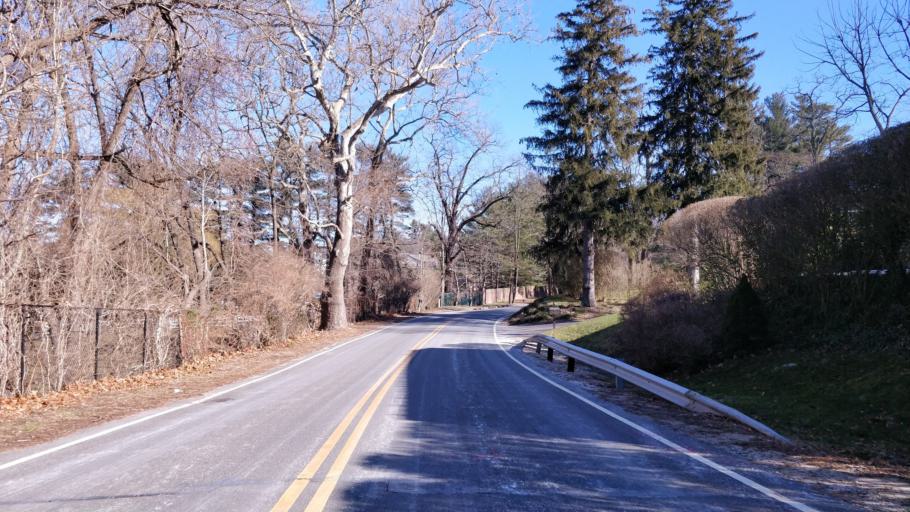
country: US
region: New York
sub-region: Nassau County
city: Brookville
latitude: 40.8069
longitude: -73.5837
